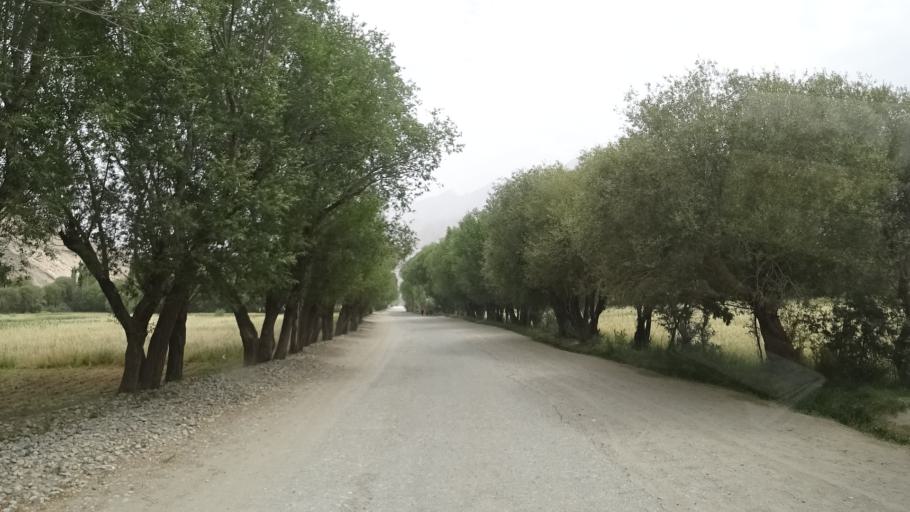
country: AF
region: Badakhshan
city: Khandud
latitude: 37.0389
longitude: 72.6545
